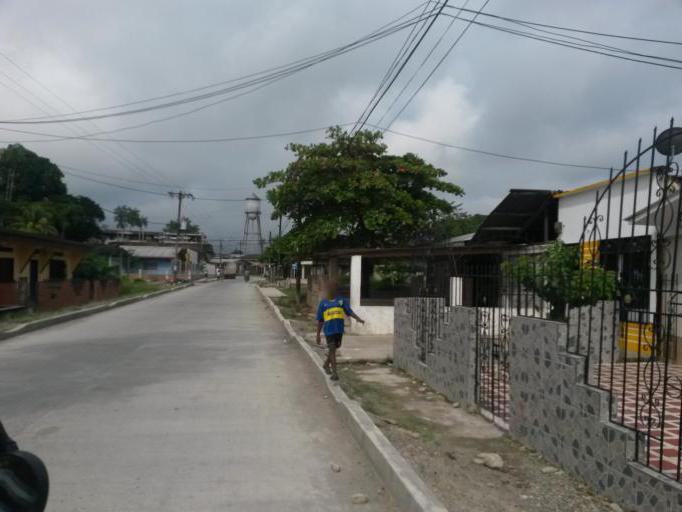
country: CO
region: Cauca
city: Guapi
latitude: 2.5732
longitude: -77.8885
